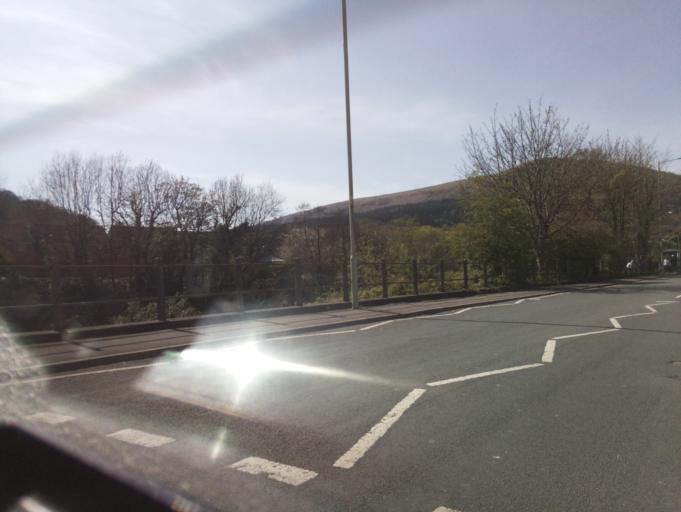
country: GB
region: Wales
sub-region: Cardiff
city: Radyr
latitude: 51.5403
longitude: -3.2644
